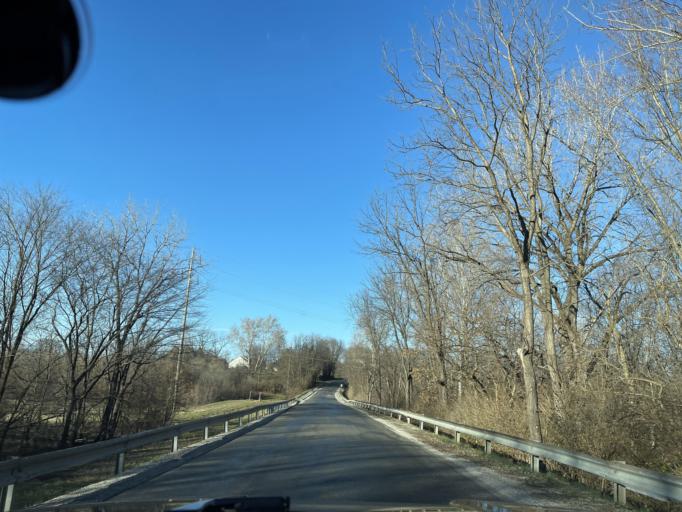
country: US
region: Illinois
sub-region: Sangamon County
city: Leland Grove
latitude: 39.8118
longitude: -89.7133
